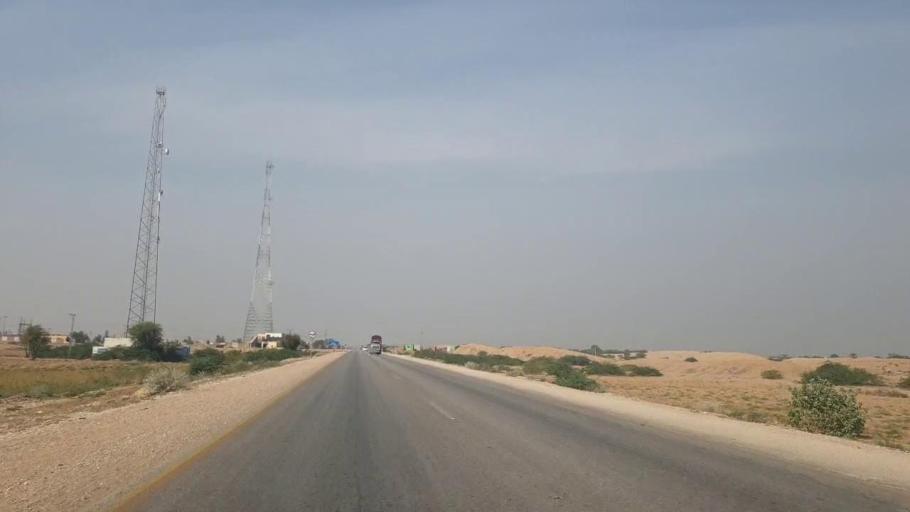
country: PK
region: Sindh
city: Sann
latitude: 26.0526
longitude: 68.1074
